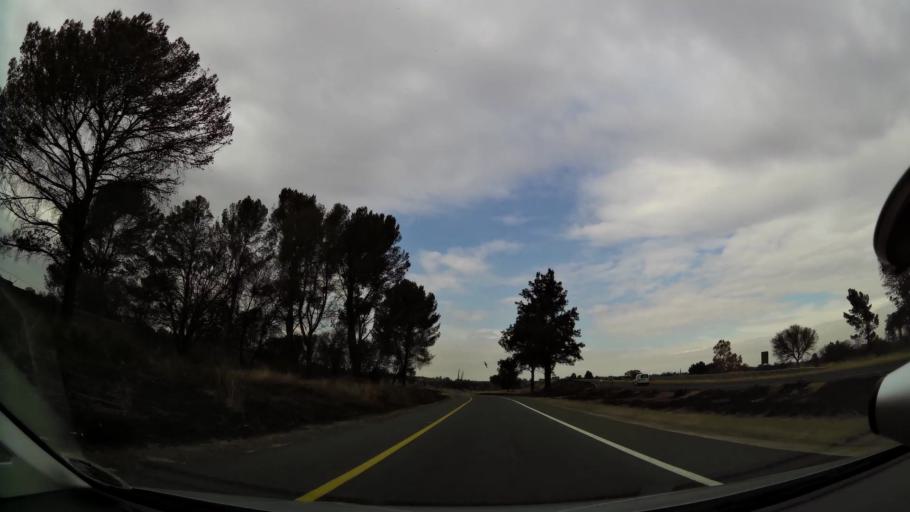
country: ZA
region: Orange Free State
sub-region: Fezile Dabi District Municipality
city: Kroonstad
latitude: -27.6551
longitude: 27.2496
